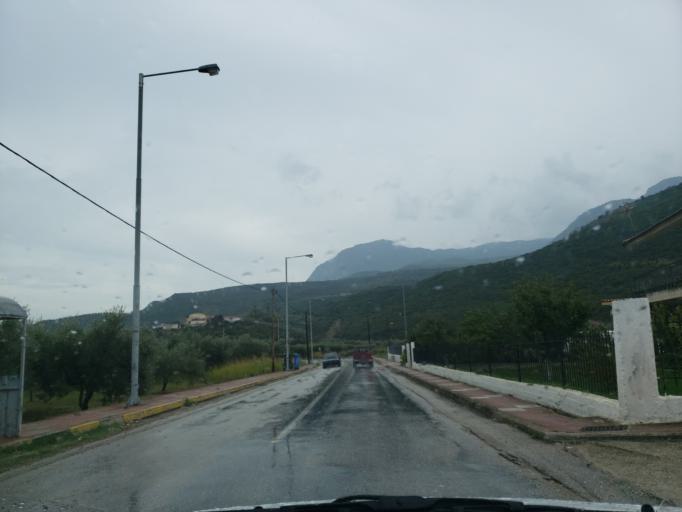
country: GR
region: Central Greece
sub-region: Nomos Fthiotidos
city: Anthili
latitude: 38.7994
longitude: 22.4716
